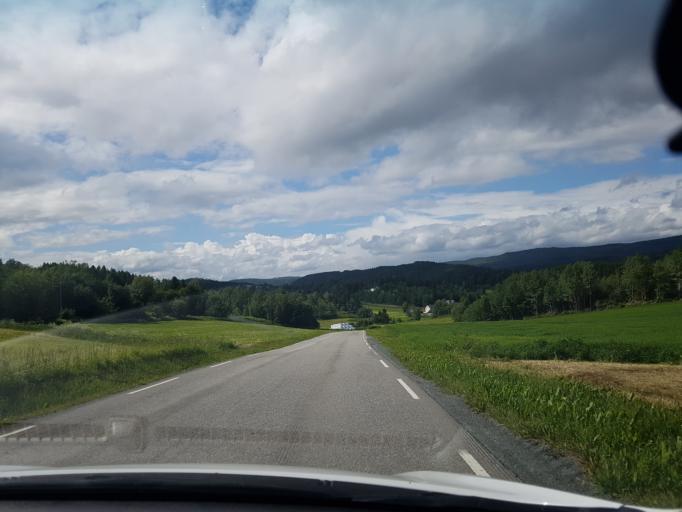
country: NO
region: Nord-Trondelag
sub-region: Stjordal
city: Stjordalshalsen
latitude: 63.5928
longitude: 10.9811
